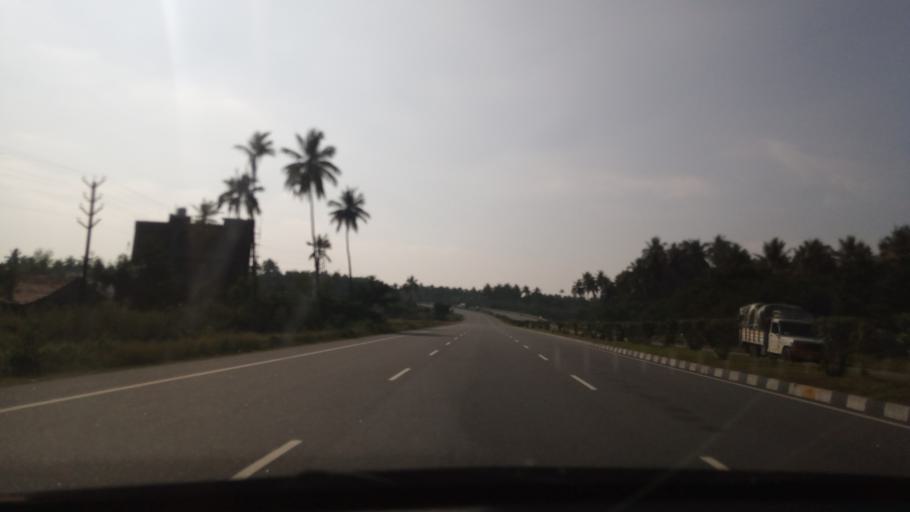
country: IN
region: Tamil Nadu
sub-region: Krishnagiri
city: Krishnagiri
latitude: 12.5514
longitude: 78.3435
